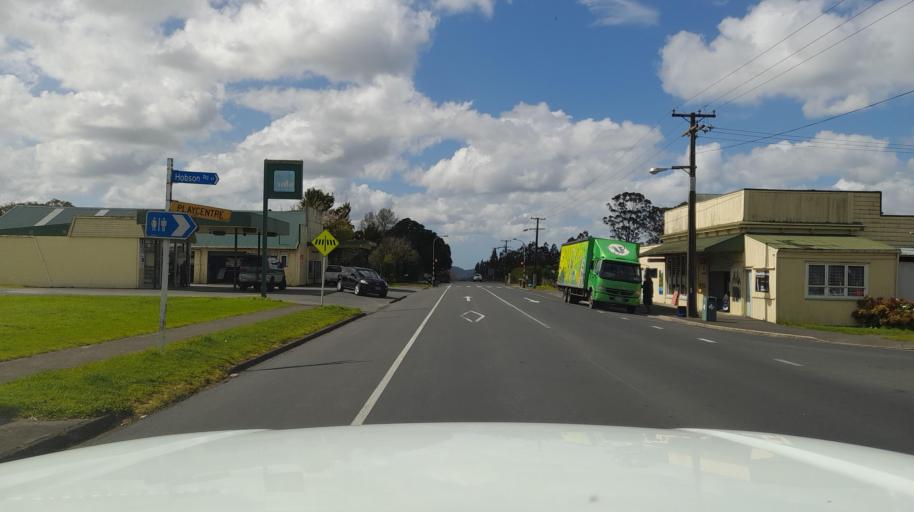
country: NZ
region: Northland
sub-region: Far North District
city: Waimate North
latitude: -35.3519
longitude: 173.8822
